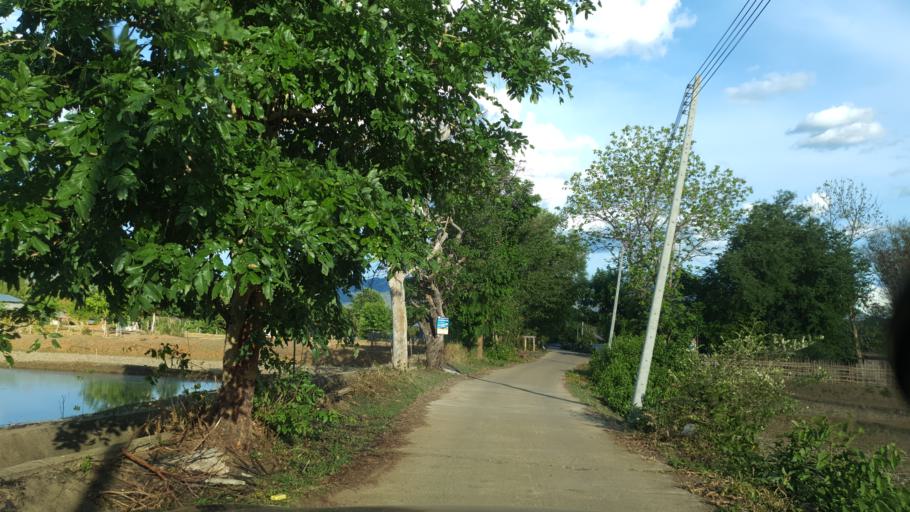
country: TH
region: Lampang
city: Sop Prap
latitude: 17.8718
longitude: 99.3062
